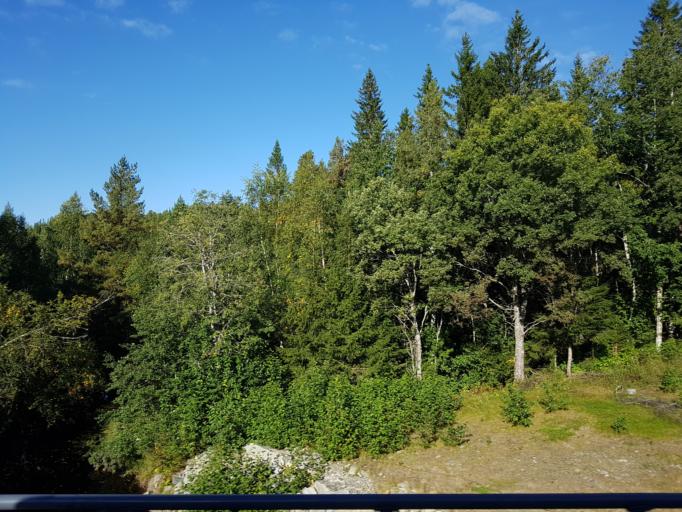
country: NO
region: Sor-Trondelag
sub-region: Trondheim
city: Trondheim
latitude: 63.6080
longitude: 10.2367
